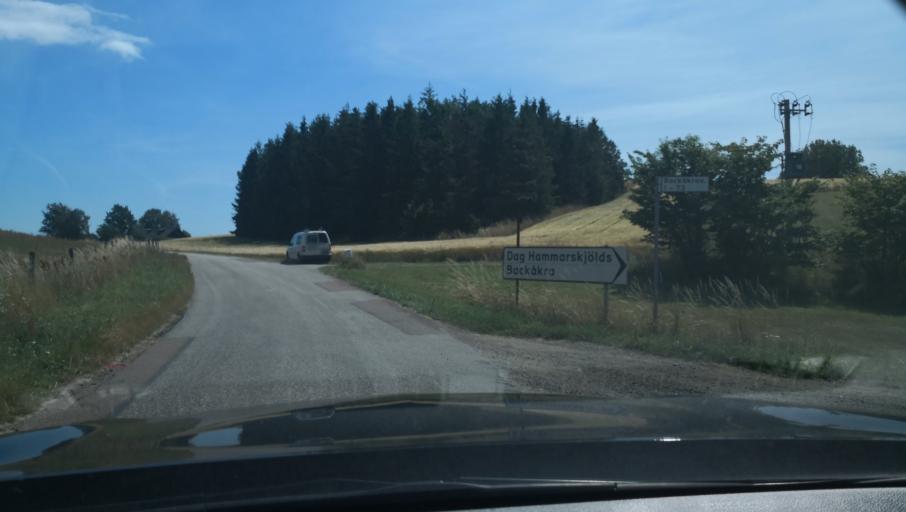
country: SE
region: Skane
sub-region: Ystads Kommun
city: Kopingebro
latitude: 55.3913
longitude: 14.1394
